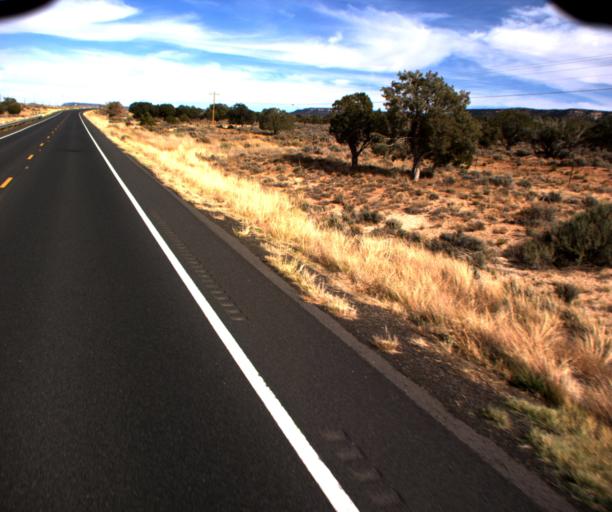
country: US
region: Arizona
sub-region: Navajo County
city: Kayenta
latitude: 36.5157
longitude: -110.5952
